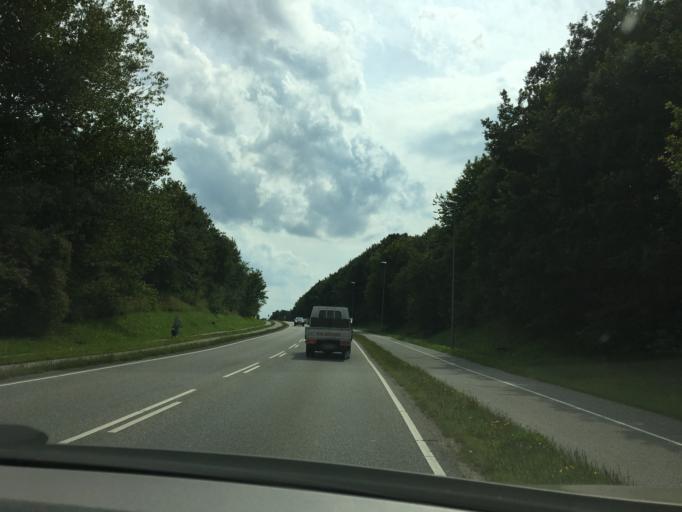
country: DK
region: Central Jutland
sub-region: Skive Kommune
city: Skive
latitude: 56.5571
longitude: 9.0242
